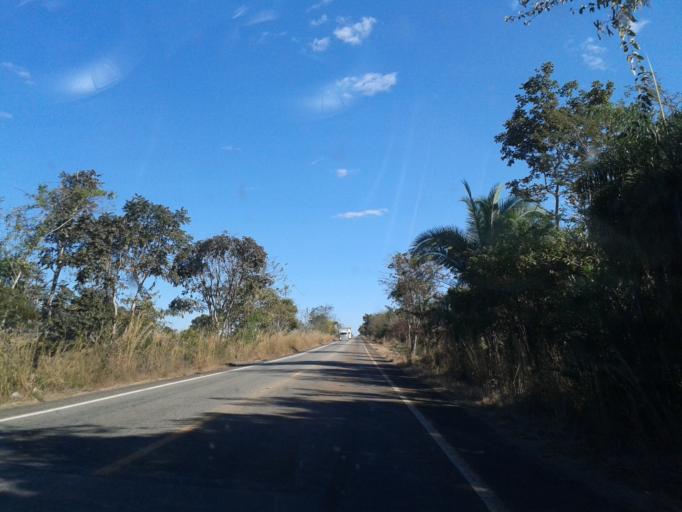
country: BR
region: Goias
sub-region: Mozarlandia
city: Mozarlandia
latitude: -14.5428
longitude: -50.4905
